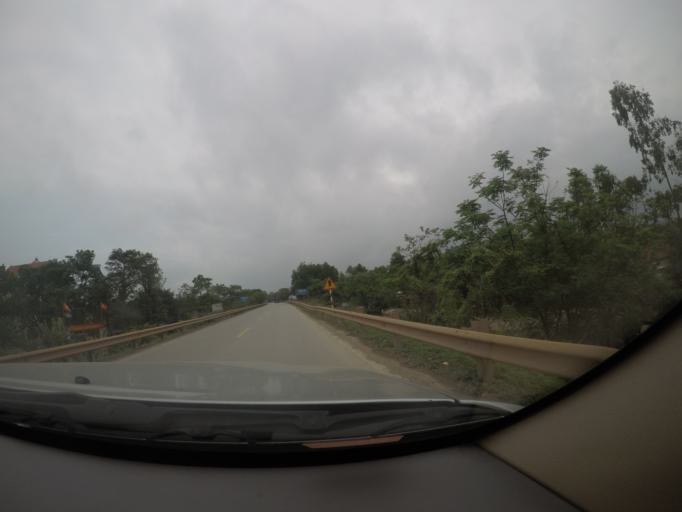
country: VN
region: Quang Binh
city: Kien Giang
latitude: 17.2310
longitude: 106.6980
